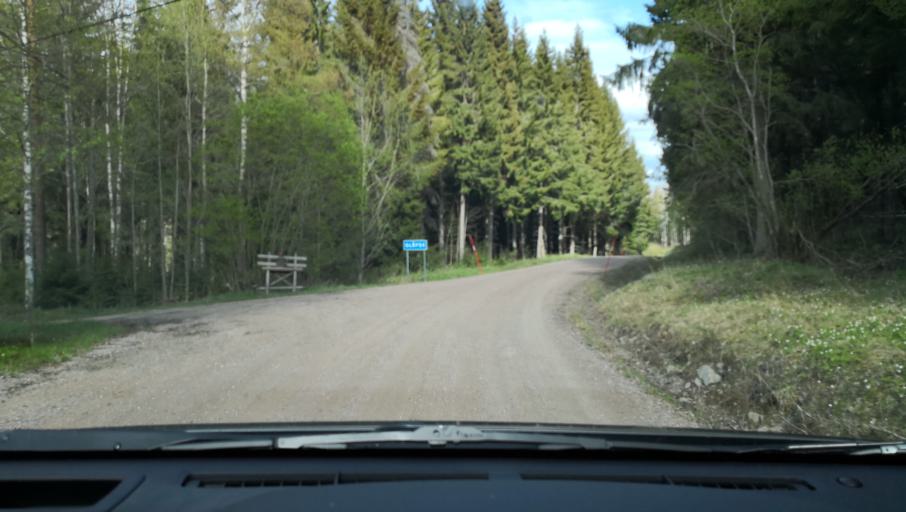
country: SE
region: Vaestmanland
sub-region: Fagersta Kommun
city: Fagersta
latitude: 60.1551
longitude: 15.6821
